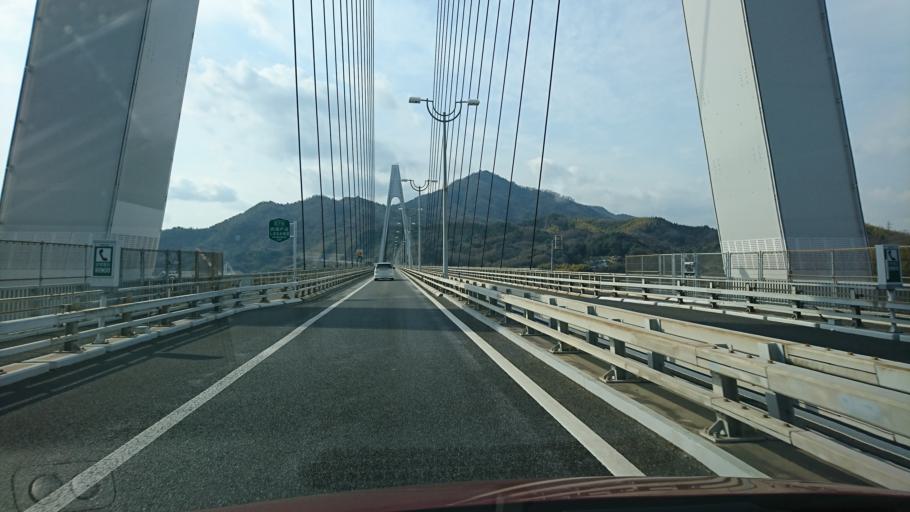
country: JP
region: Hiroshima
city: Innoshima
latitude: 34.3057
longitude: 133.1525
